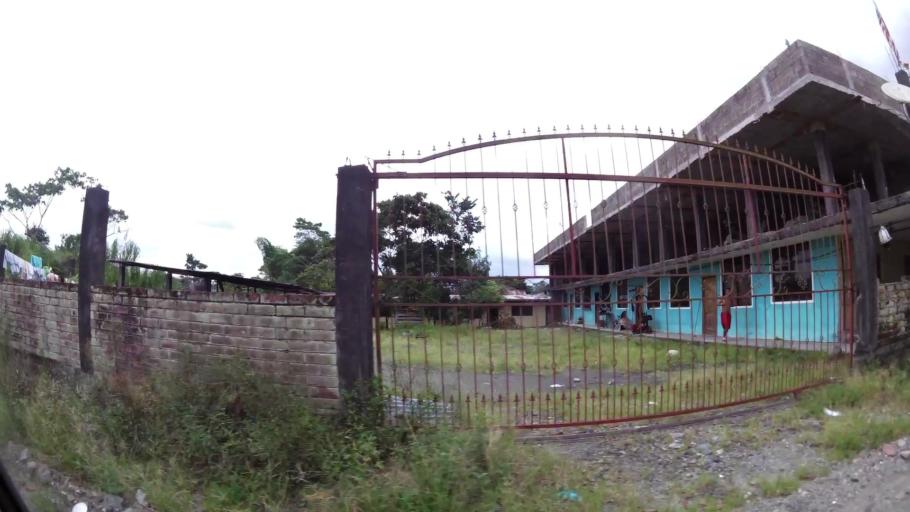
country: EC
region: Pastaza
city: Puyo
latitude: -1.4947
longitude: -78.0115
